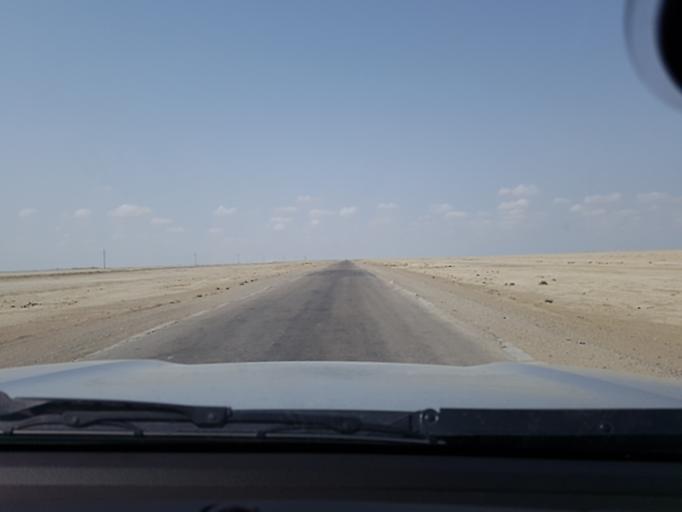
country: TM
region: Balkan
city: Gumdag
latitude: 38.6475
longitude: 54.3820
